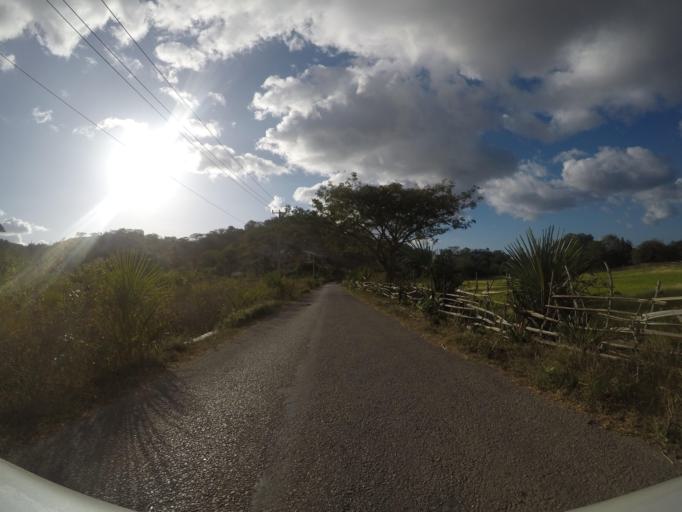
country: TL
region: Lautem
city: Lospalos
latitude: -8.4176
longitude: 126.8272
